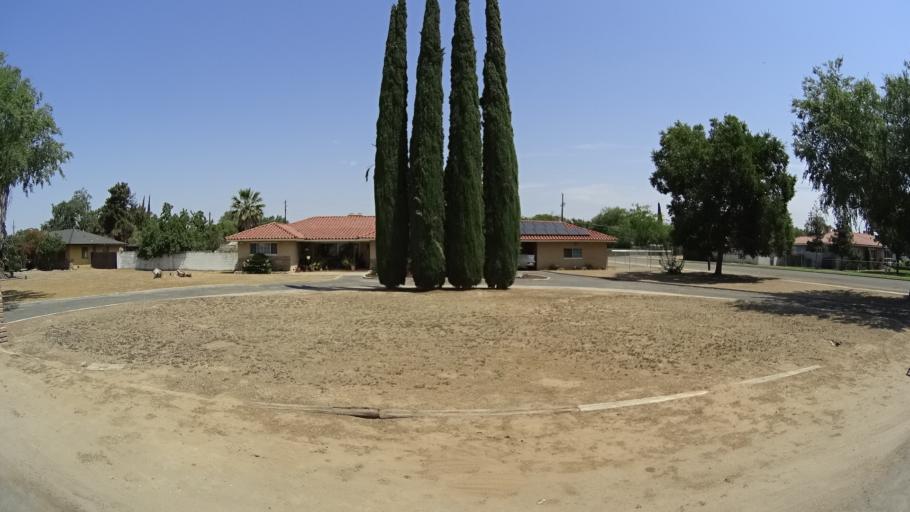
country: US
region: California
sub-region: Fresno County
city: West Park
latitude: 36.7287
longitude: -119.8327
